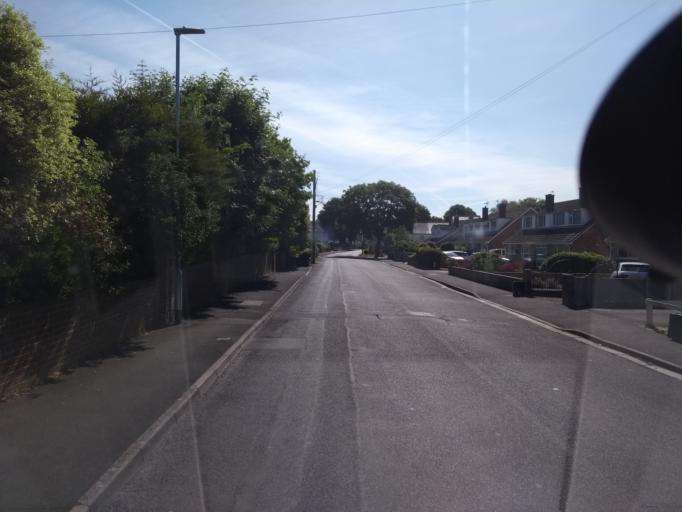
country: GB
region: England
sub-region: Somerset
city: Burnham-on-Sea
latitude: 51.2458
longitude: -2.9898
